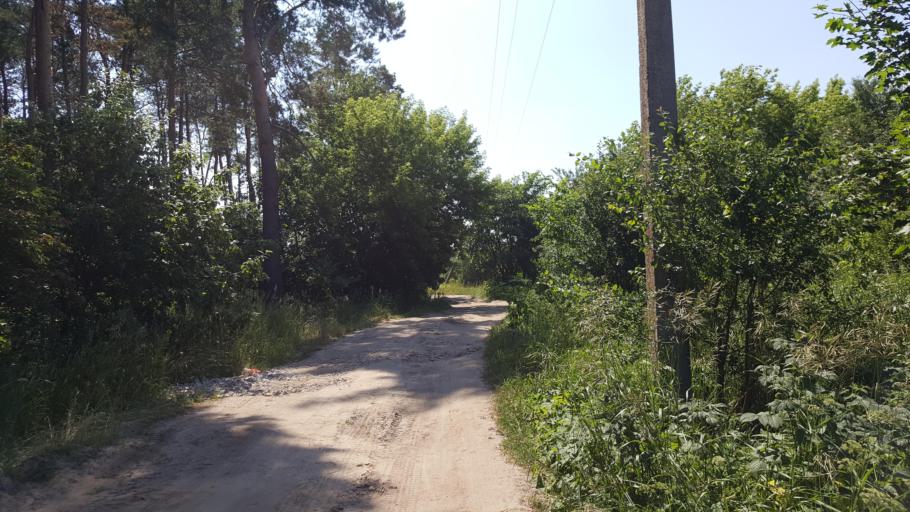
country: BY
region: Brest
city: Kamyanyets
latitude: 52.4083
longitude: 23.8387
